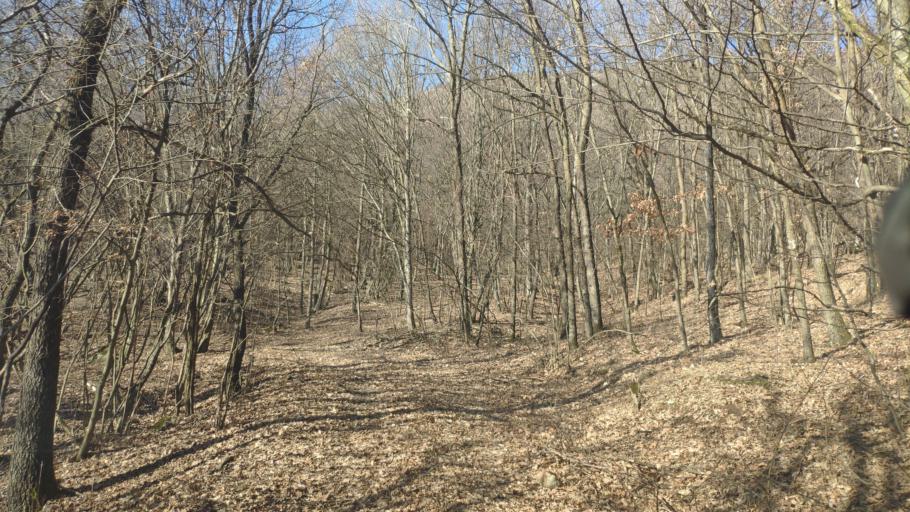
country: SK
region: Kosicky
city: Roznava
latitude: 48.6037
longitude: 20.7204
